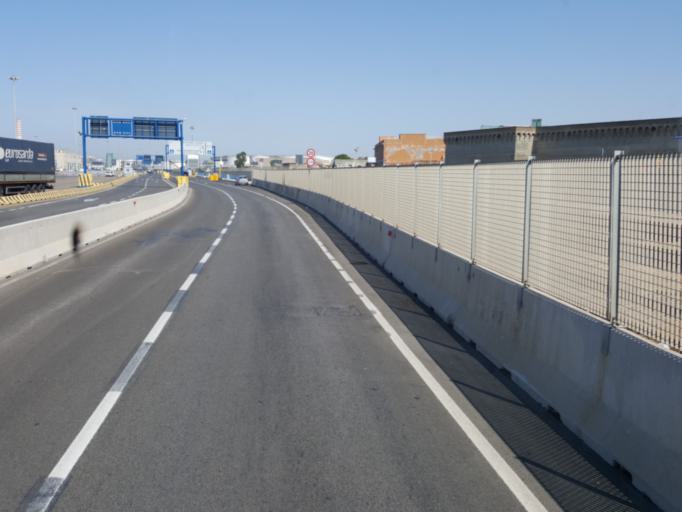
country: IT
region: Latium
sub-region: Citta metropolitana di Roma Capitale
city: Civitavecchia
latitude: 42.0979
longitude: 11.7852
